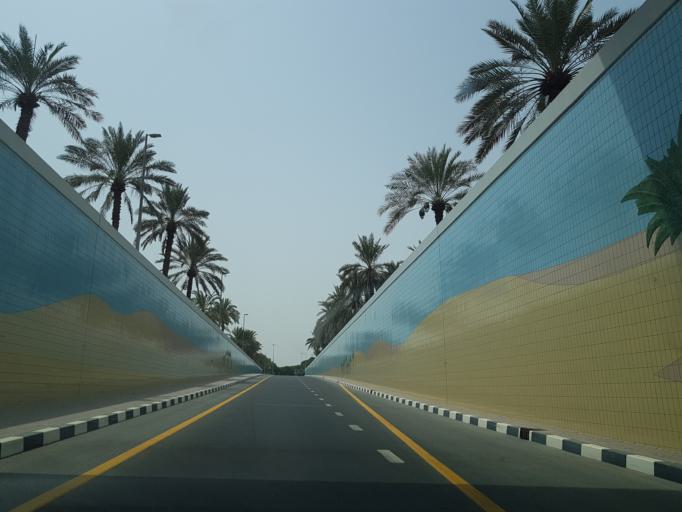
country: AE
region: Ash Shariqah
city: Sharjah
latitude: 25.2306
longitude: 55.2988
